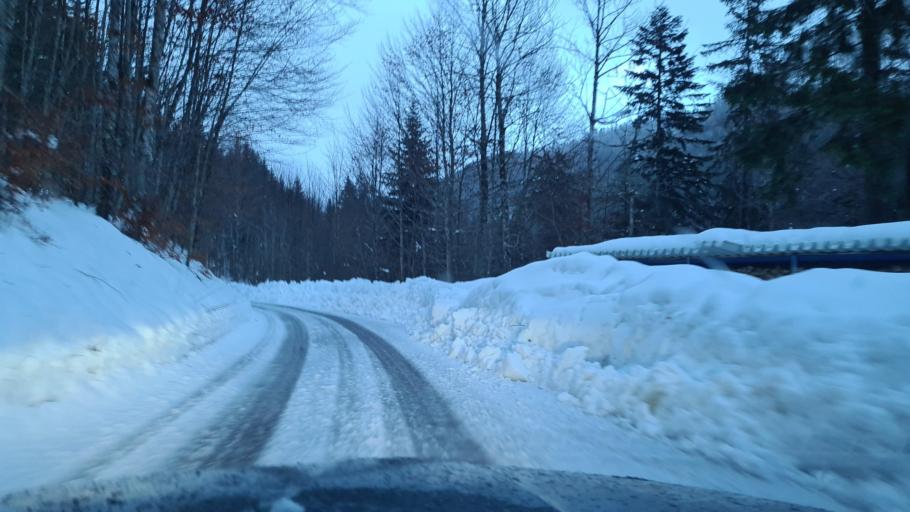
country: AT
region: Salzburg
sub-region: Politischer Bezirk Sankt Johann im Pongau
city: Werfen
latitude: 47.4813
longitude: 13.1524
